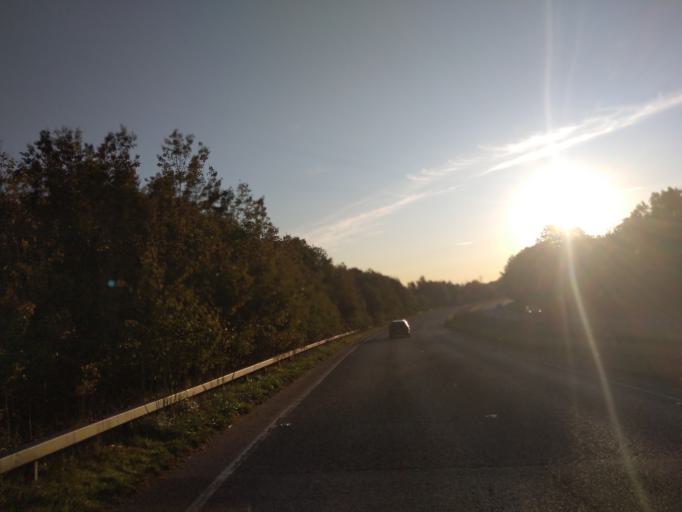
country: GB
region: England
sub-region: West Sussex
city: Rustington
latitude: 50.8240
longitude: -0.5166
